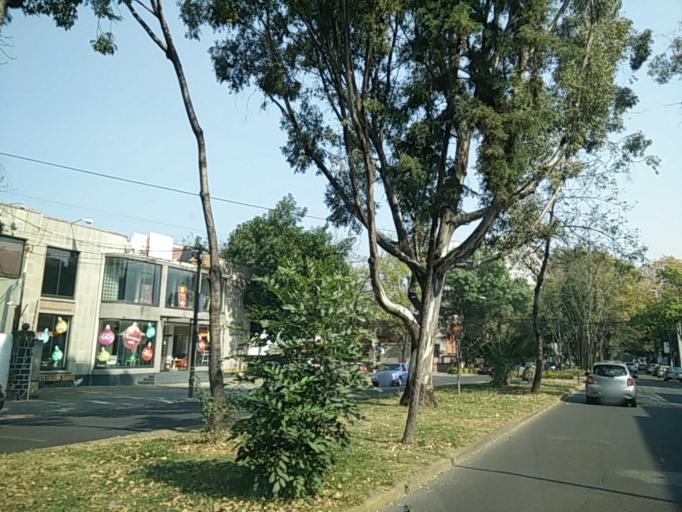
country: MX
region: Mexico City
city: Miguel Hidalgo
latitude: 19.4358
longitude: -99.1961
